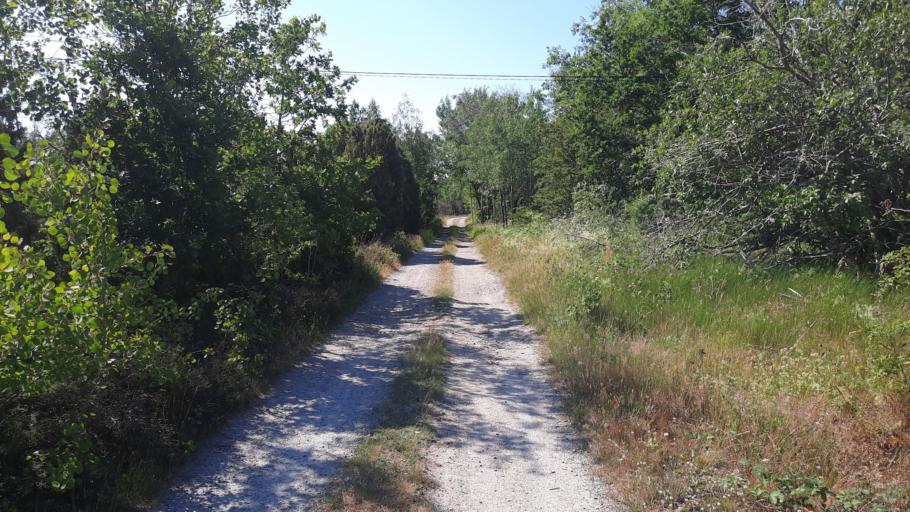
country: SE
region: Blekinge
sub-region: Karlskrona Kommun
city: Sturko
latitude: 56.1140
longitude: 15.6597
